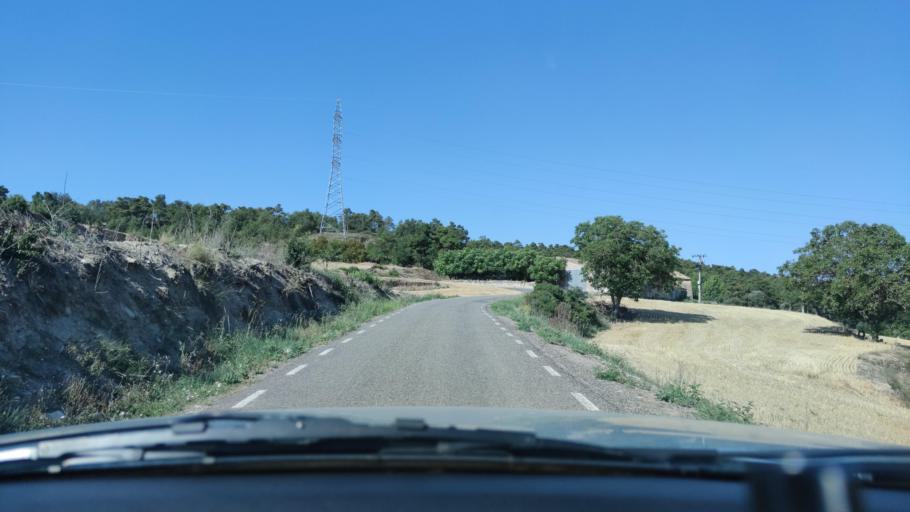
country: ES
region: Catalonia
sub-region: Provincia de Barcelona
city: Pujalt
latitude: 41.7087
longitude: 1.3787
